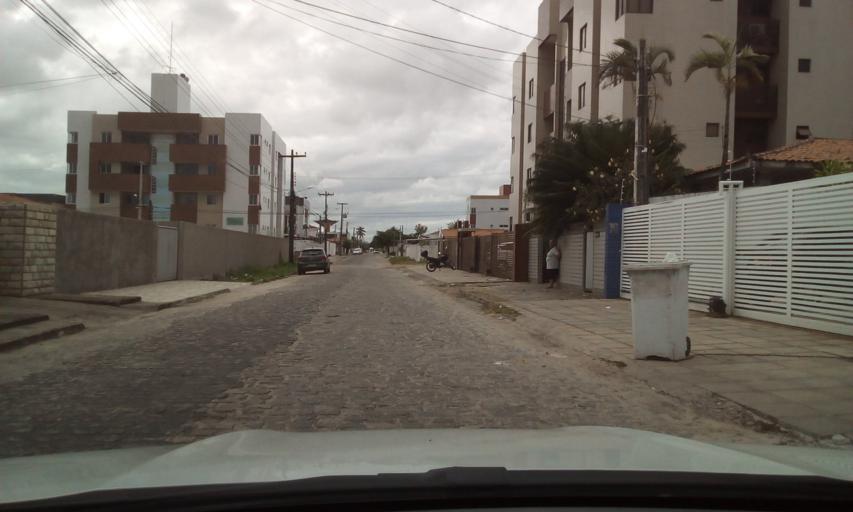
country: BR
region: Paraiba
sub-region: Joao Pessoa
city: Joao Pessoa
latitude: -7.1596
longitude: -34.8683
